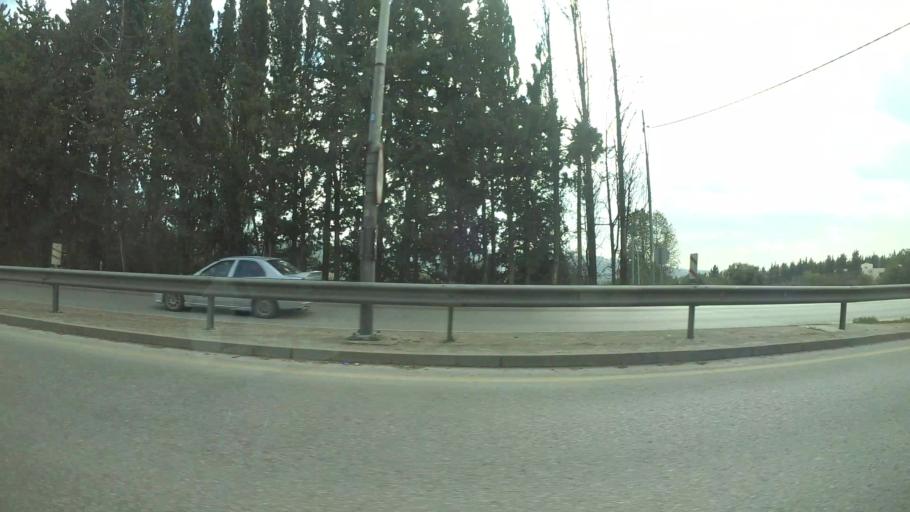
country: JO
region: Amman
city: Al Jubayhah
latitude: 32.0283
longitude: 35.8137
